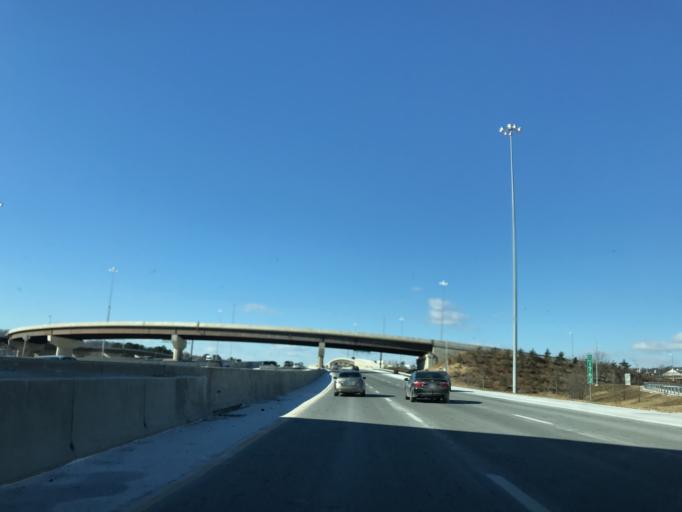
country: US
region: Virginia
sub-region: Fairfax County
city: Huntington
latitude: 38.8001
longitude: -77.0736
